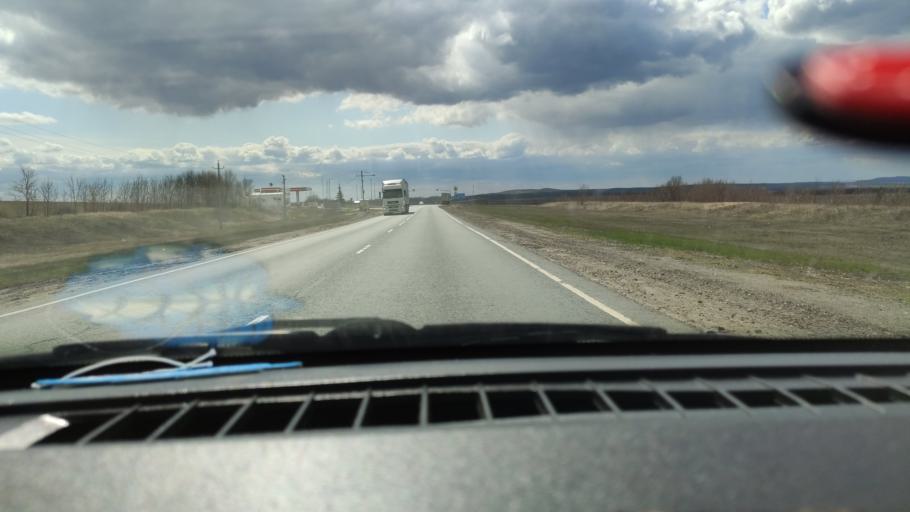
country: RU
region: Saratov
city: Alekseyevka
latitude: 52.2923
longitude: 47.9294
